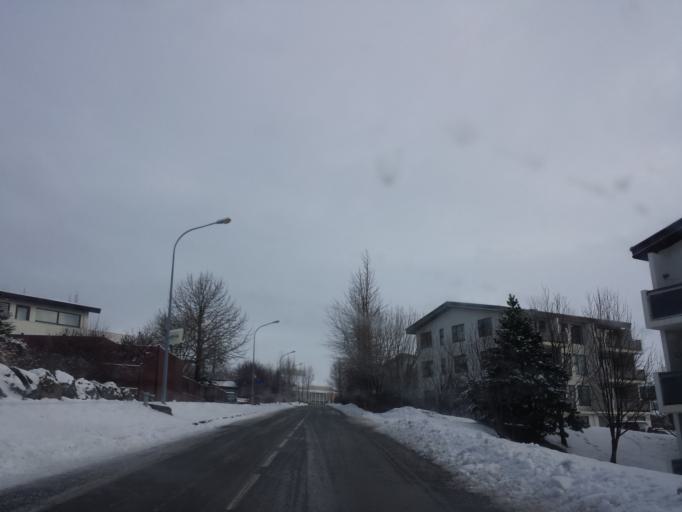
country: IS
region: Capital Region
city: Reykjavik
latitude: 64.1083
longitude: -21.8703
